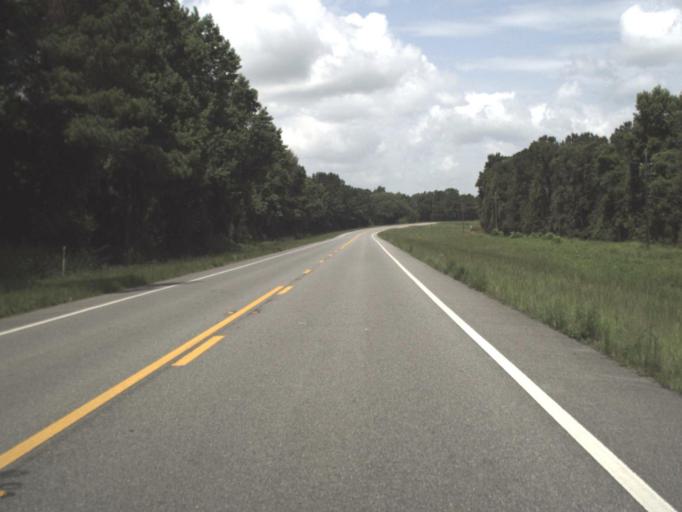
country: US
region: Florida
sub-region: Madison County
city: Madison
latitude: 30.4692
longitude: -83.5788
